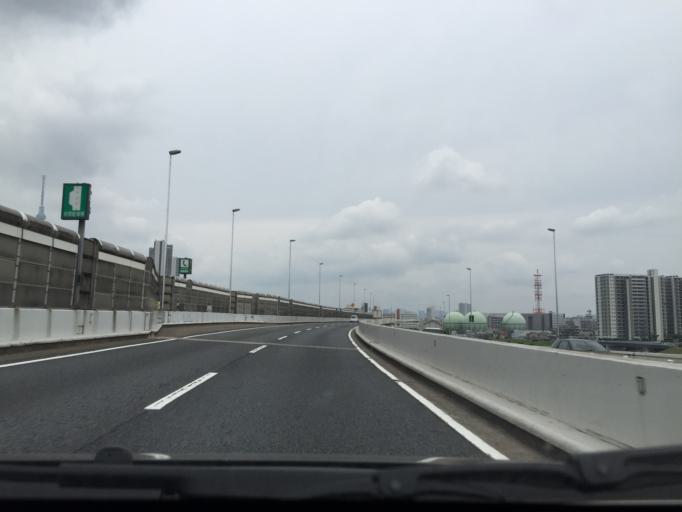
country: JP
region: Saitama
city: Soka
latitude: 35.7352
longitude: 139.8148
